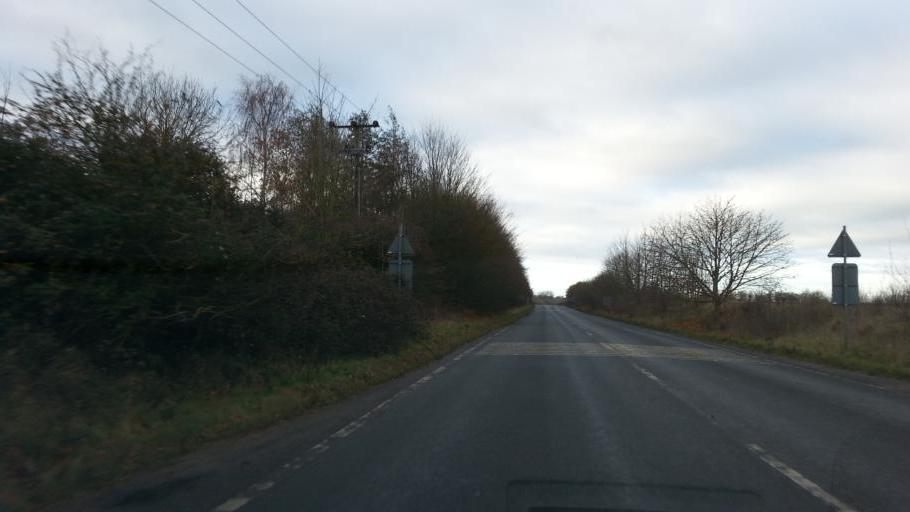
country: GB
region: England
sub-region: Suffolk
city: Ixworth
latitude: 52.3033
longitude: 0.8437
